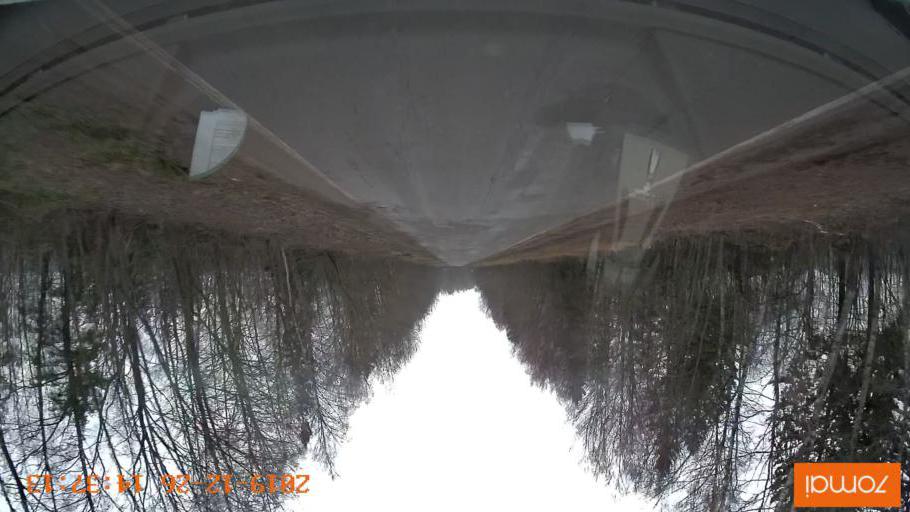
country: RU
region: Jaroslavl
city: Poshekhon'ye
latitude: 58.4040
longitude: 38.9730
